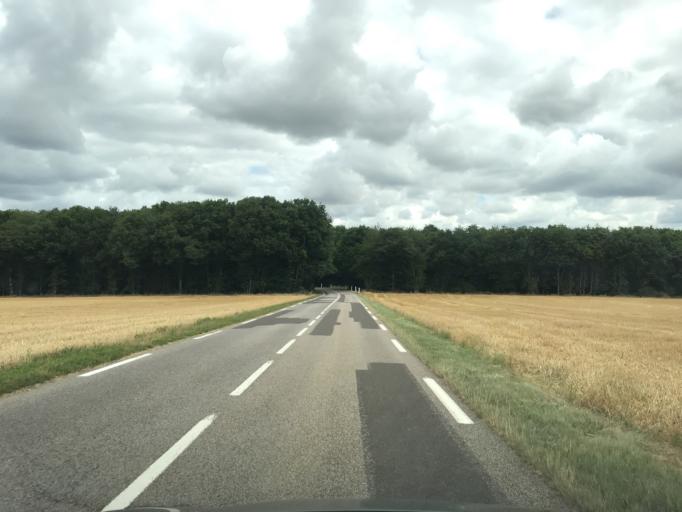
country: FR
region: Haute-Normandie
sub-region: Departement de l'Eure
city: Menilles
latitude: 49.0352
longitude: 1.2897
